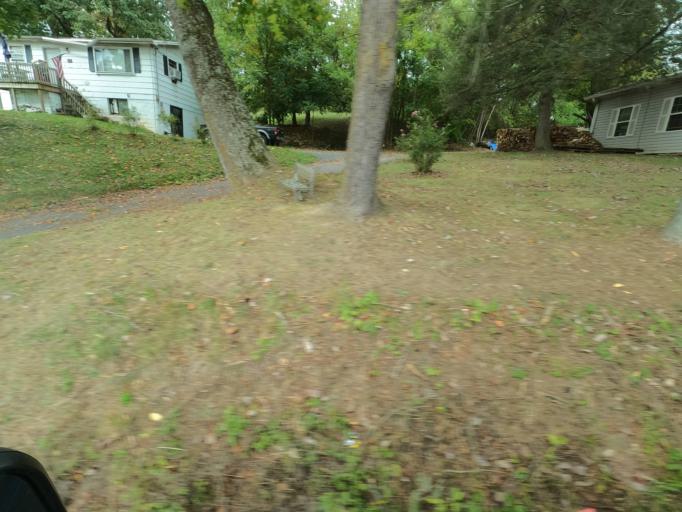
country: US
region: Tennessee
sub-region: Washington County
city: Jonesborough
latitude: 36.2510
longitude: -82.5434
